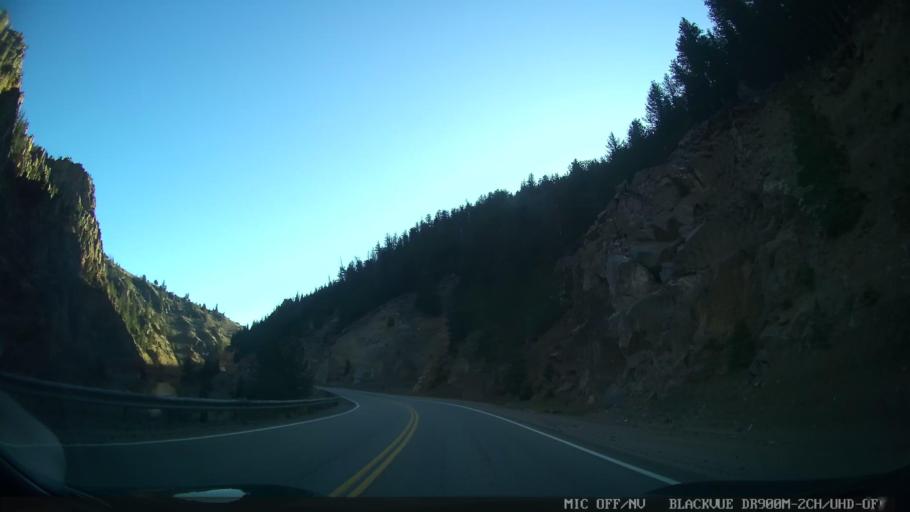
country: US
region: Colorado
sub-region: Grand County
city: Hot Sulphur Springs
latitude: 40.0620
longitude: -106.1259
